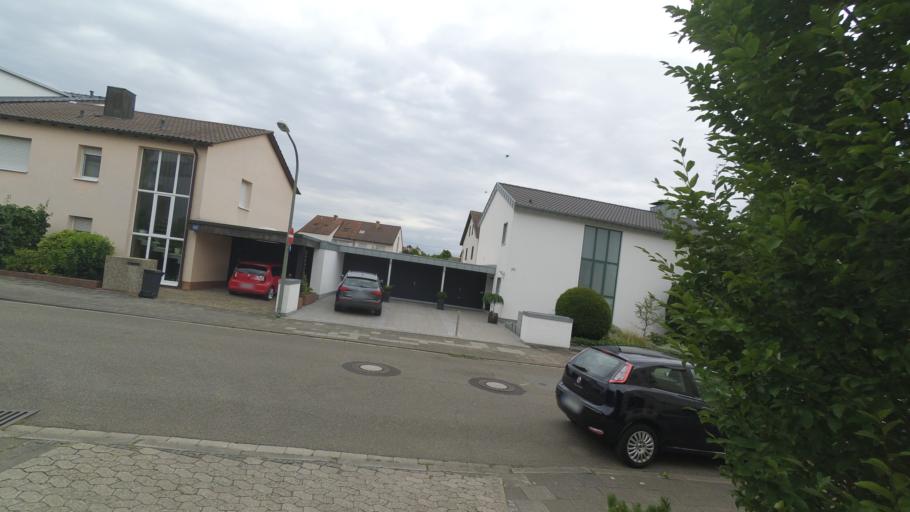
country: DE
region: Rheinland-Pfalz
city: Neuhofen
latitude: 49.4412
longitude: 8.4181
